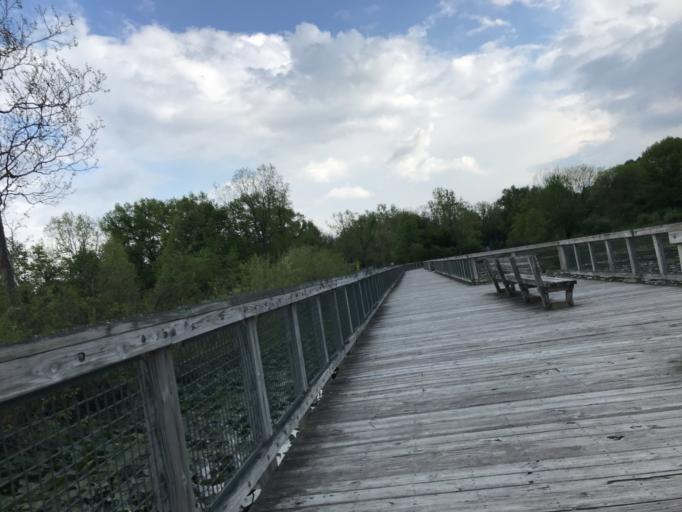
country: US
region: Michigan
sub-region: Oakland County
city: South Lyon
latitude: 42.5268
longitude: -83.6715
